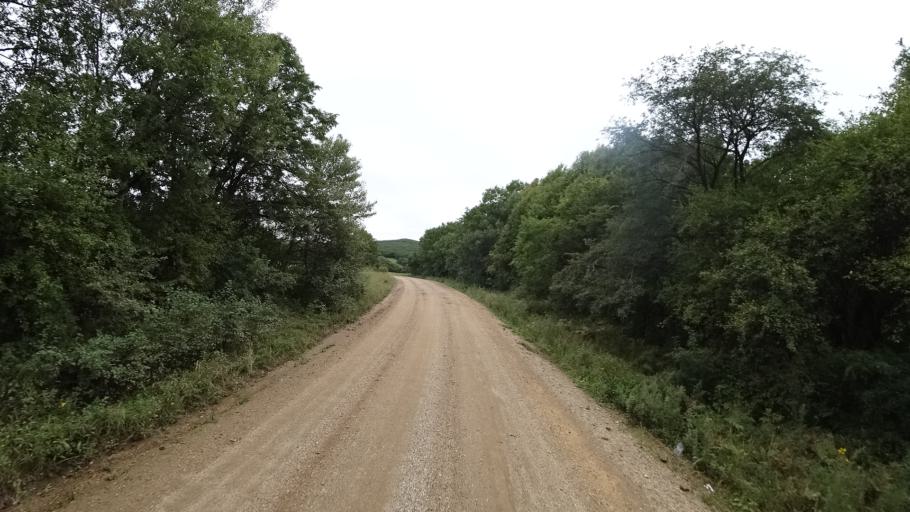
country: RU
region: Primorskiy
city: Lyalichi
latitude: 44.0595
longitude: 132.4769
